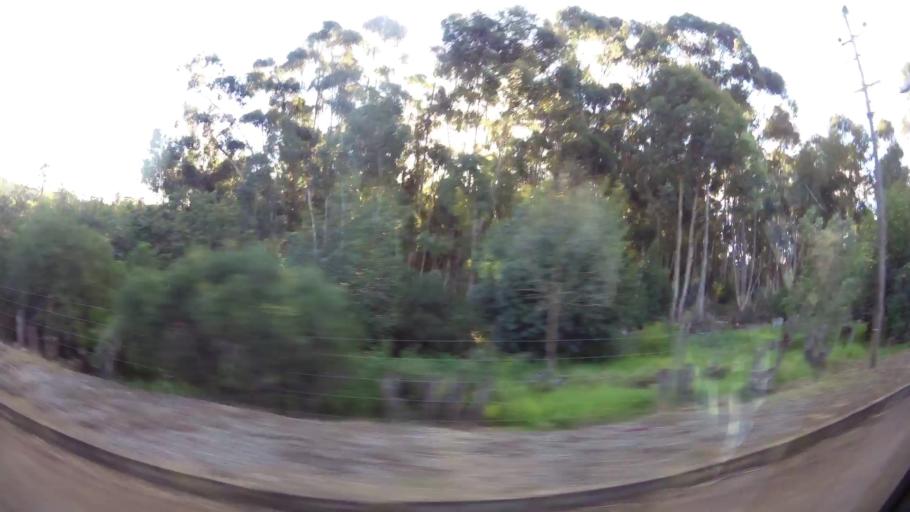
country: ZA
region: Western Cape
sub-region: Eden District Municipality
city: Riversdale
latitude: -34.0834
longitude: 20.9492
